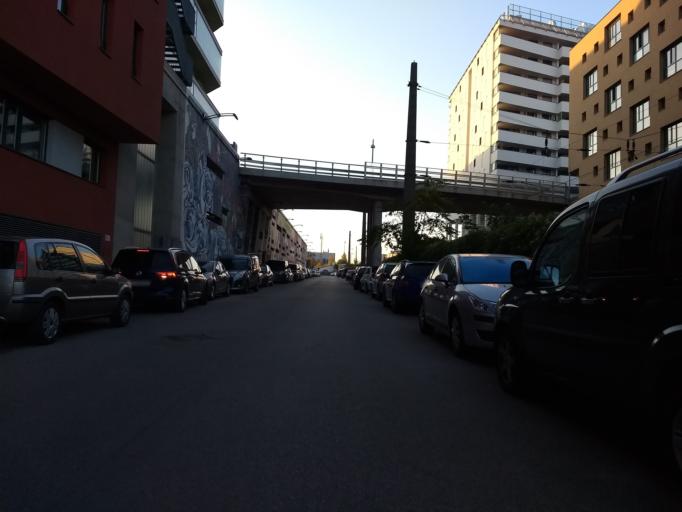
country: AT
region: Lower Austria
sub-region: Politischer Bezirk Modling
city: Vosendorf
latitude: 48.1665
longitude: 16.3273
